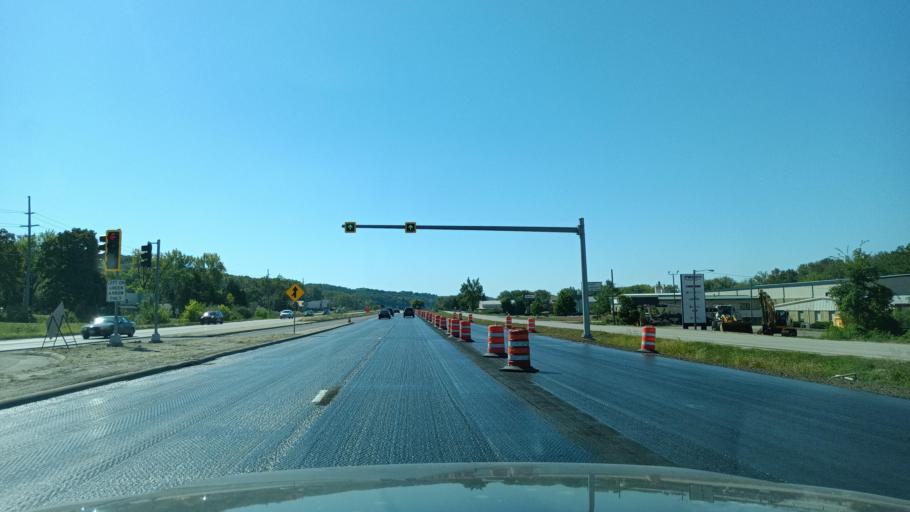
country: US
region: Illinois
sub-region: Peoria County
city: North Peoria
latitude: 40.7068
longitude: -89.5345
